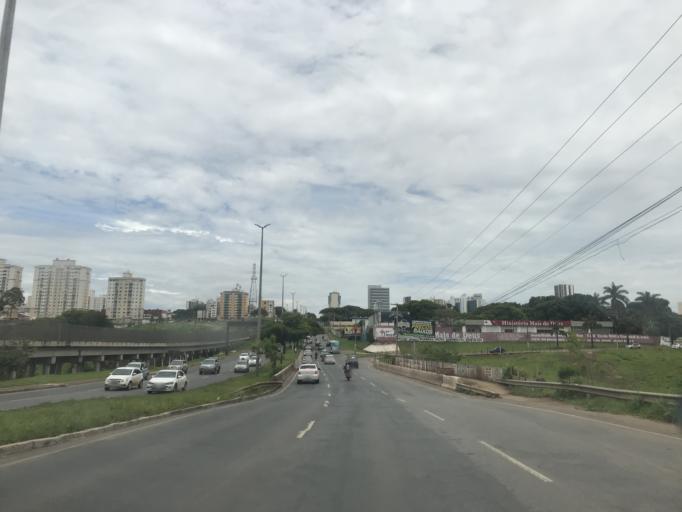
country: BR
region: Federal District
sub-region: Brasilia
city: Brasilia
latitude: -15.8364
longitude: -48.0653
